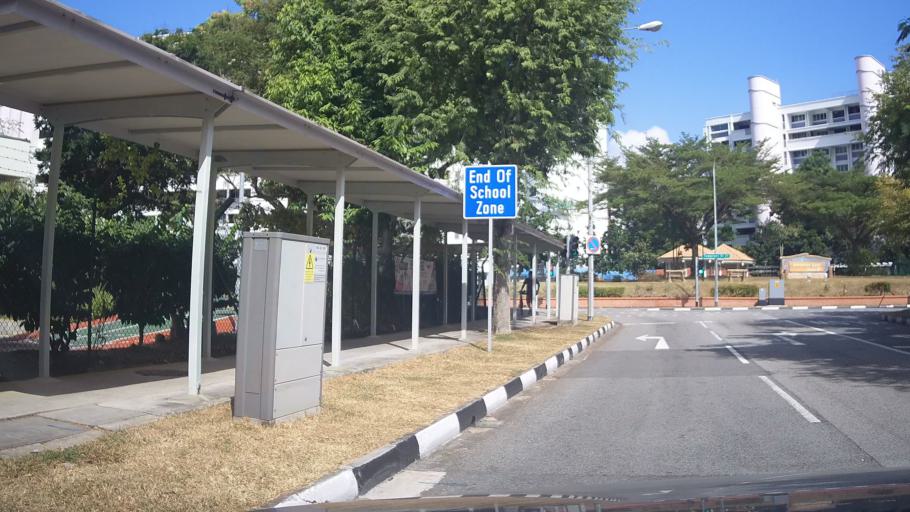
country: SG
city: Singapore
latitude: 1.3515
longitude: 103.9511
